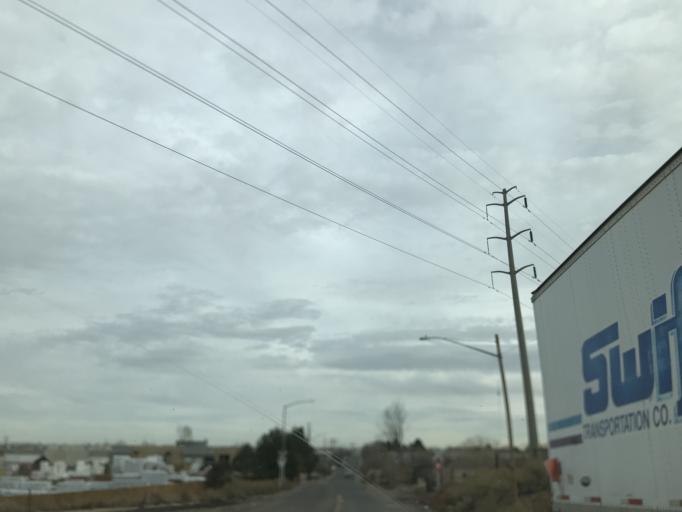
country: US
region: Colorado
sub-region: Adams County
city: Commerce City
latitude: 39.7838
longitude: -104.9164
